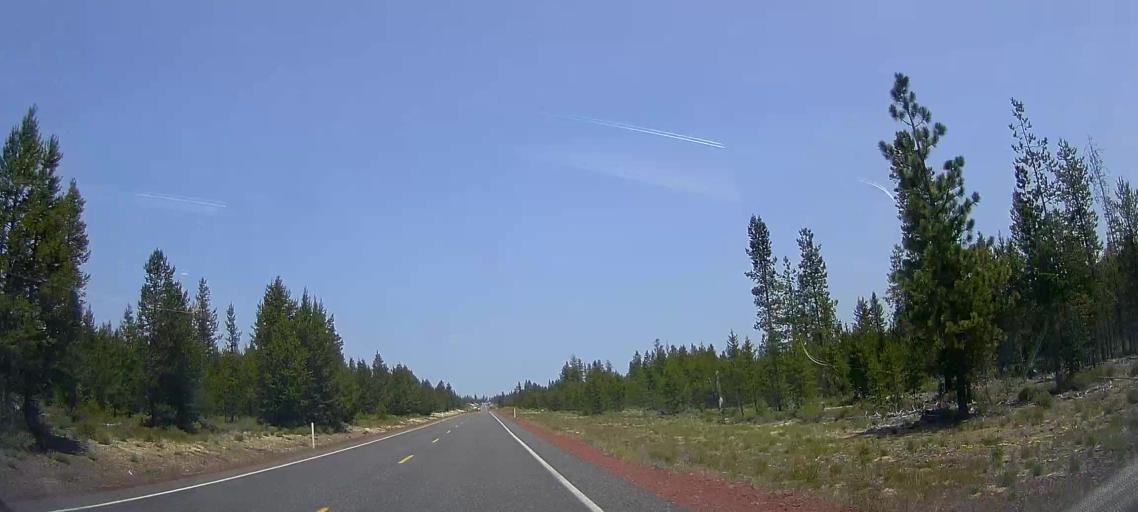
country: US
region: Oregon
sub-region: Deschutes County
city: La Pine
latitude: 43.3923
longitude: -121.7275
